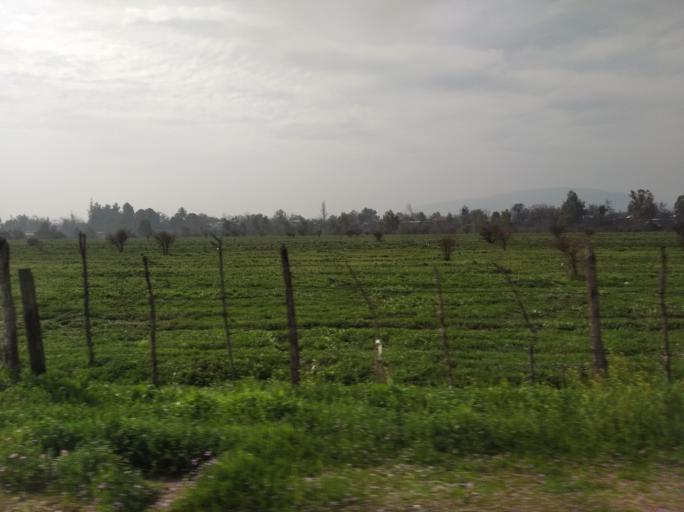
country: CL
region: Santiago Metropolitan
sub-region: Provincia de Chacabuco
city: Lampa
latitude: -33.1714
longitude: -70.8945
